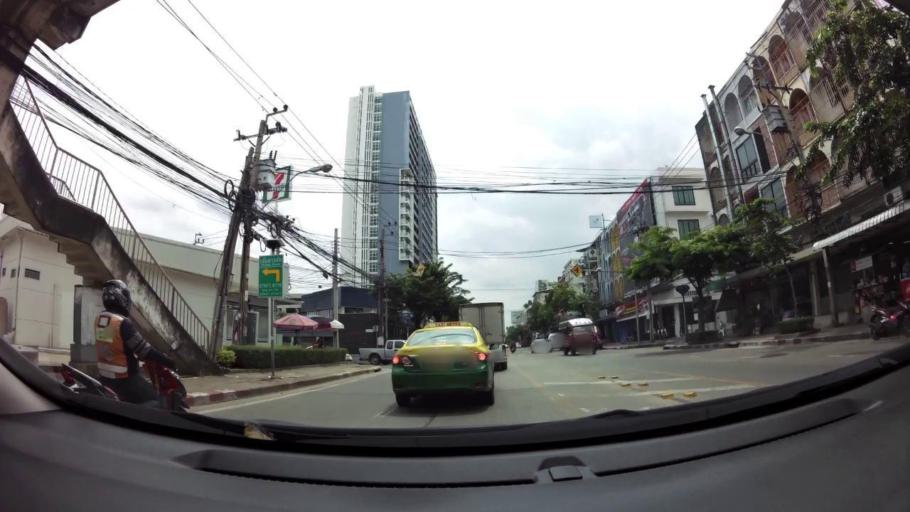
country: TH
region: Bangkok
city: Phra Khanong
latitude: 13.6787
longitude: 100.6136
